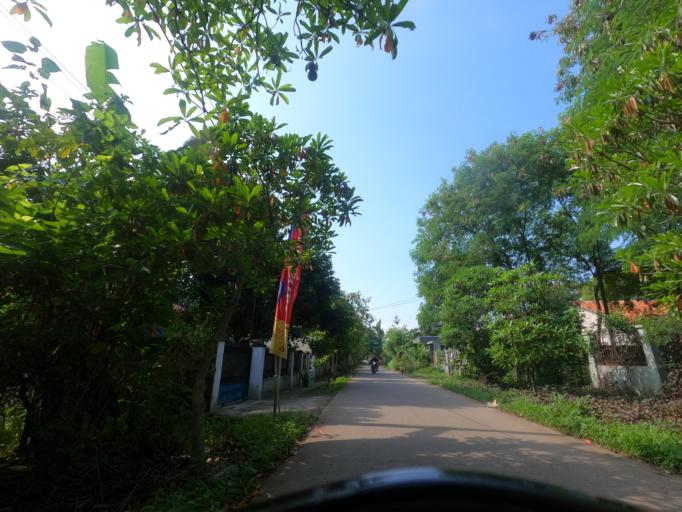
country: ID
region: West Java
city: Lembang
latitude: -6.5784
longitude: 107.7825
